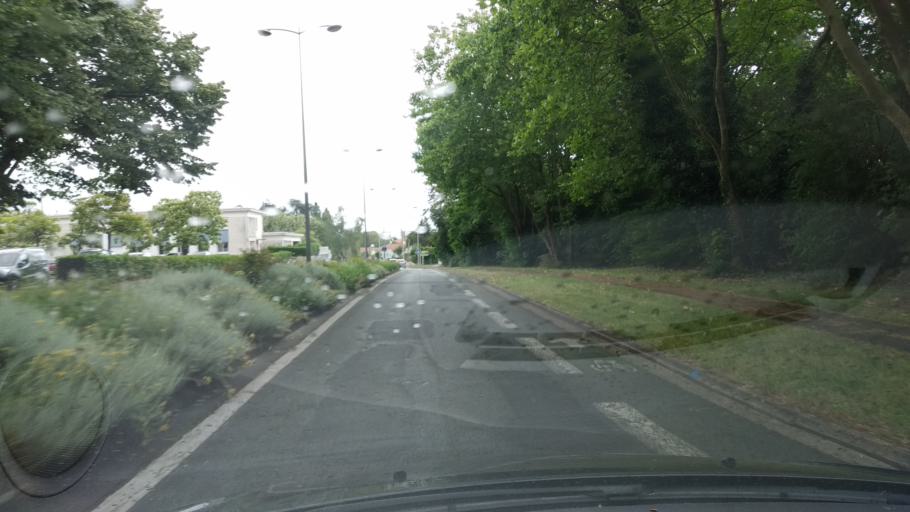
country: FR
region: Poitou-Charentes
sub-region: Departement de la Vienne
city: Saint-Benoit
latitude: 46.5646
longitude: 0.3441
